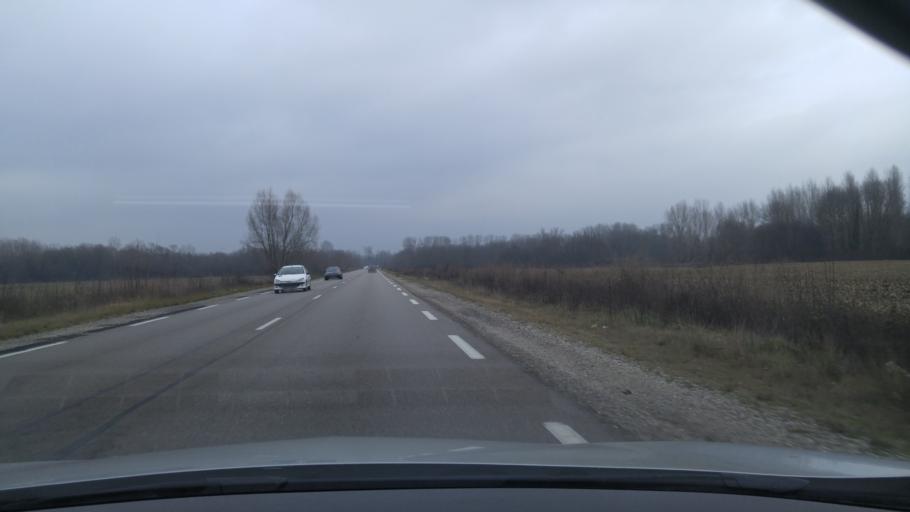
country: FR
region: Rhone-Alpes
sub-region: Departement de l'Isere
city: La Verpilliere
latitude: 45.6436
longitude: 5.1485
